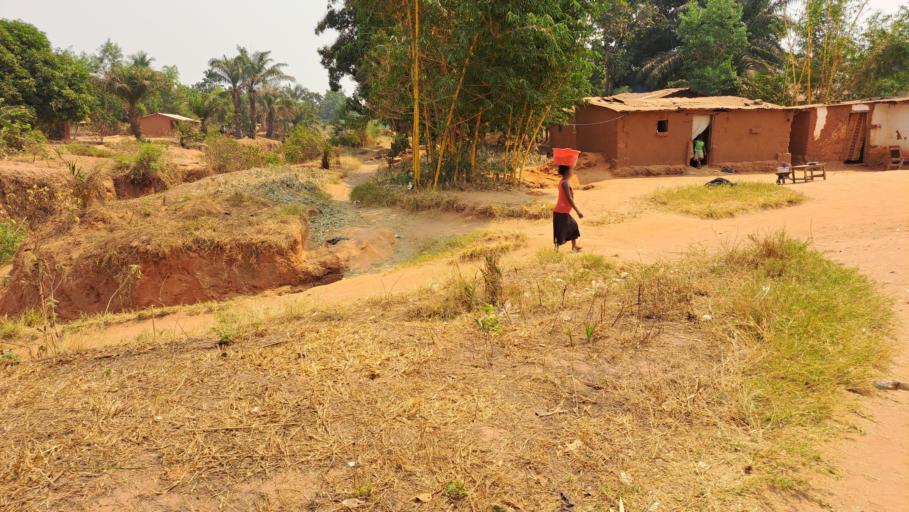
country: CD
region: Kasai-Oriental
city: Mbuji-Mayi
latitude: -6.0982
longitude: 23.5609
